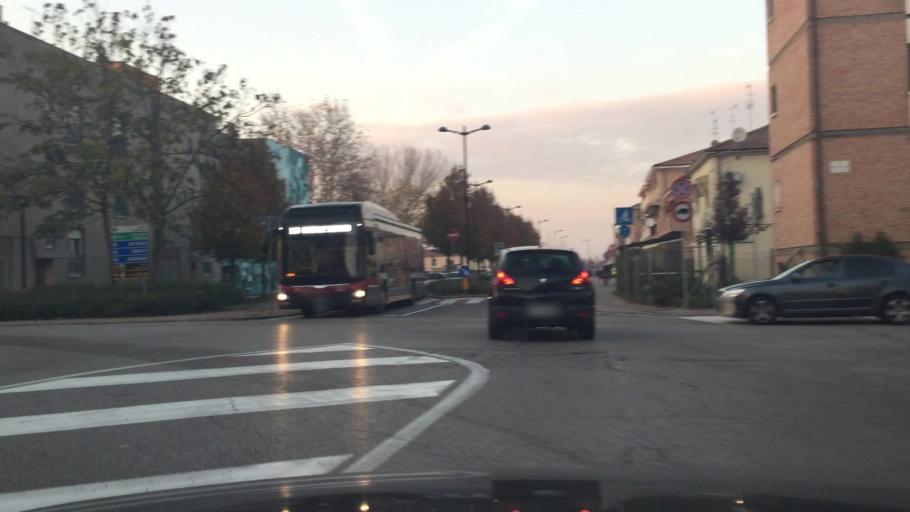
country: IT
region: Emilia-Romagna
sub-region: Provincia di Ferrara
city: Ferrara
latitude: 44.8611
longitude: 11.6075
